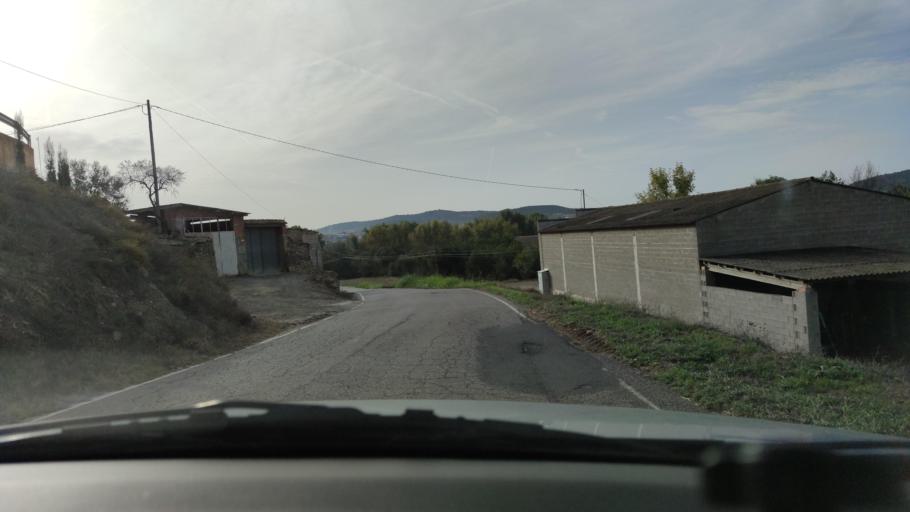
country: ES
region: Catalonia
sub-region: Provincia de Lleida
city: Artesa de Segre
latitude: 41.9050
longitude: 1.0398
